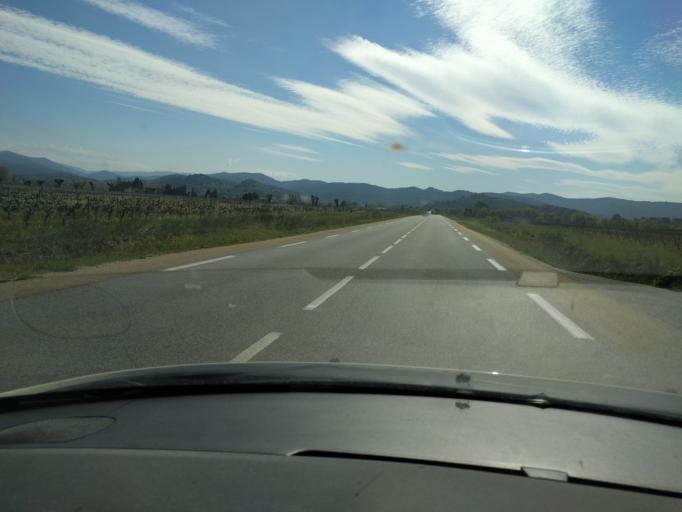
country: FR
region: Provence-Alpes-Cote d'Azur
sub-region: Departement du Var
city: Pierrefeu-du-Var
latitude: 43.2317
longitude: 6.1086
